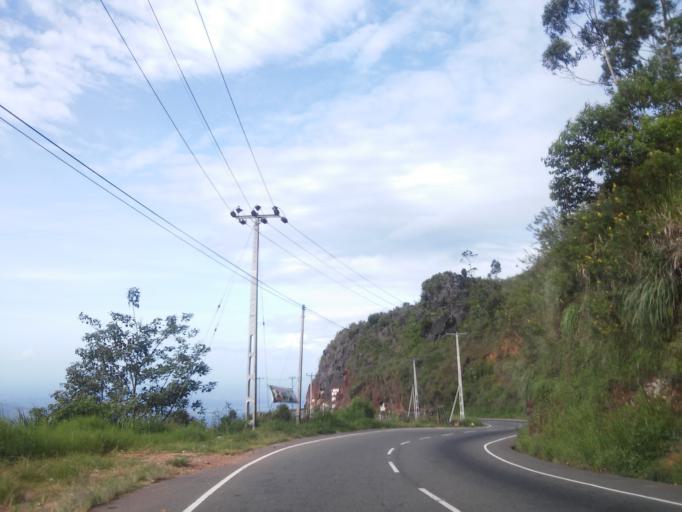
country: LK
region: Uva
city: Haputale
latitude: 6.7614
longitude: 80.9486
